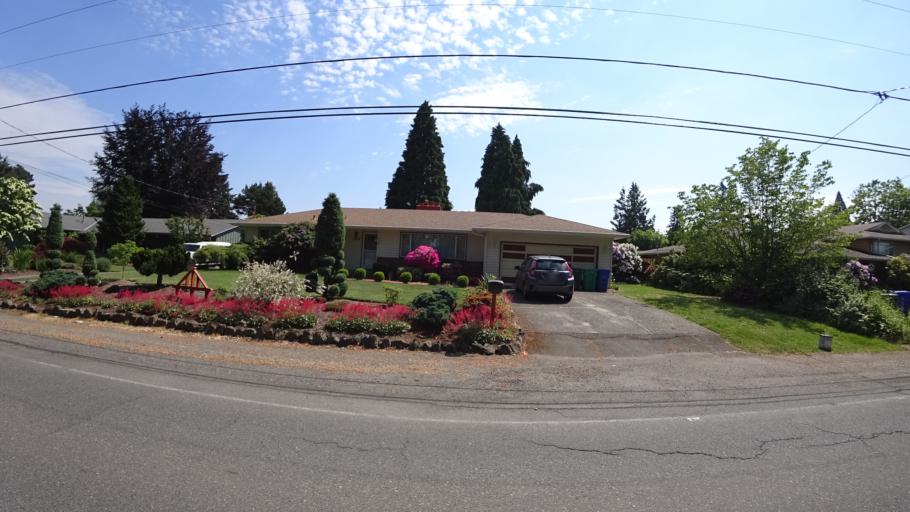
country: US
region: Oregon
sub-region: Multnomah County
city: Fairview
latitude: 45.5379
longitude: -122.5130
